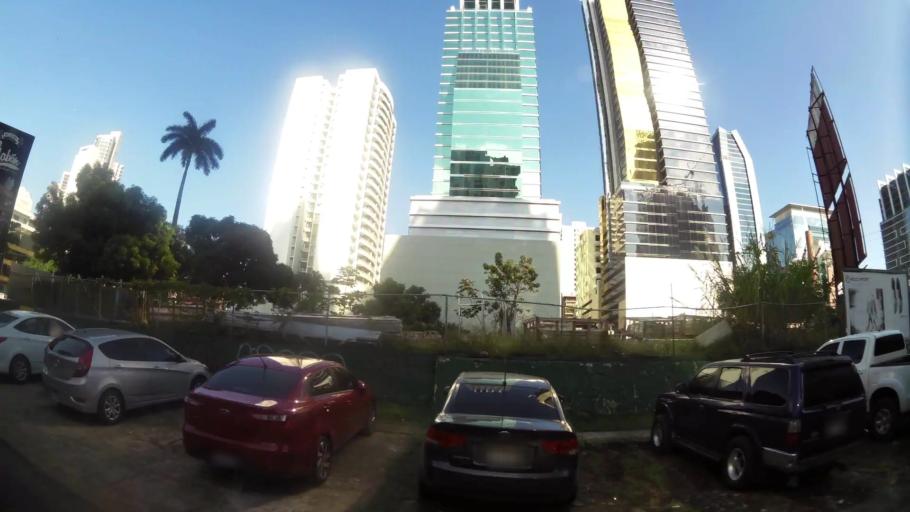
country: PA
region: Panama
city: Panama
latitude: 8.9837
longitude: -79.5208
